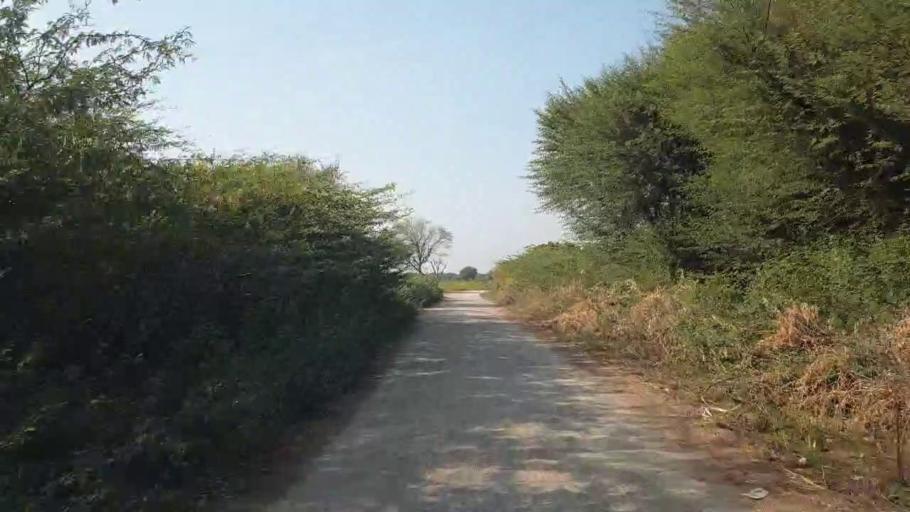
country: PK
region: Sindh
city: Mirpur Khas
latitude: 25.4138
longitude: 68.9182
